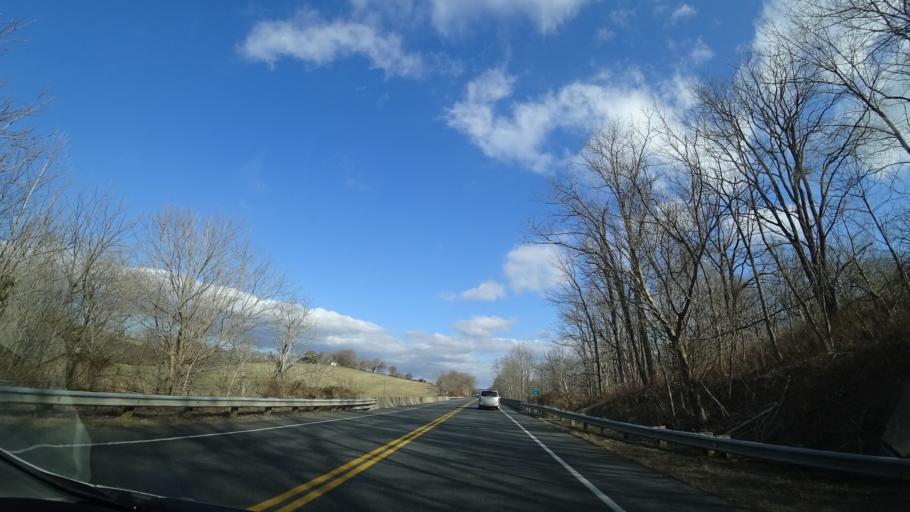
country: US
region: Virginia
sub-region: Fauquier County
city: Marshall
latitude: 38.9295
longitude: -77.9318
